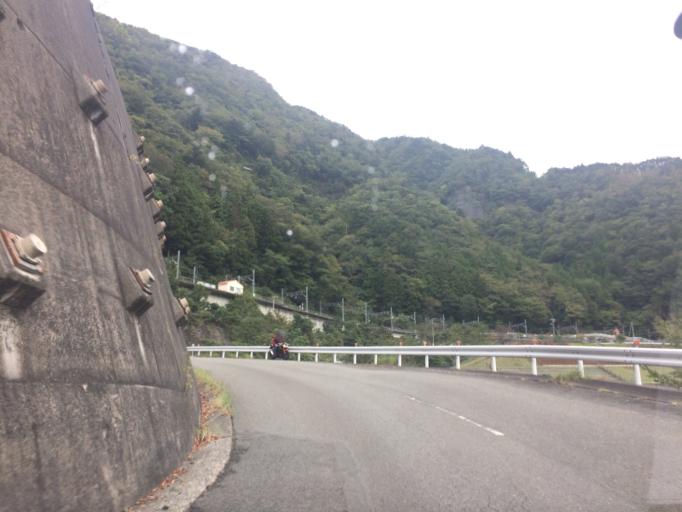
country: JP
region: Shizuoka
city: Shizuoka-shi
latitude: 35.1690
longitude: 138.1536
